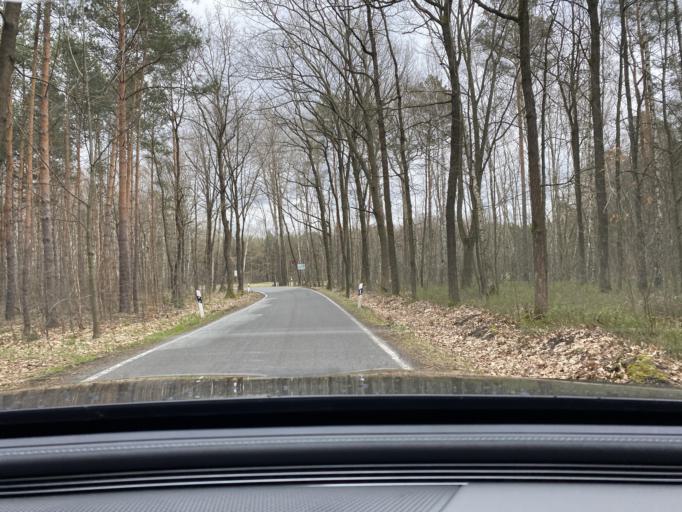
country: DE
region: Saxony
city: Uhyst
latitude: 51.3263
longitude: 14.4747
